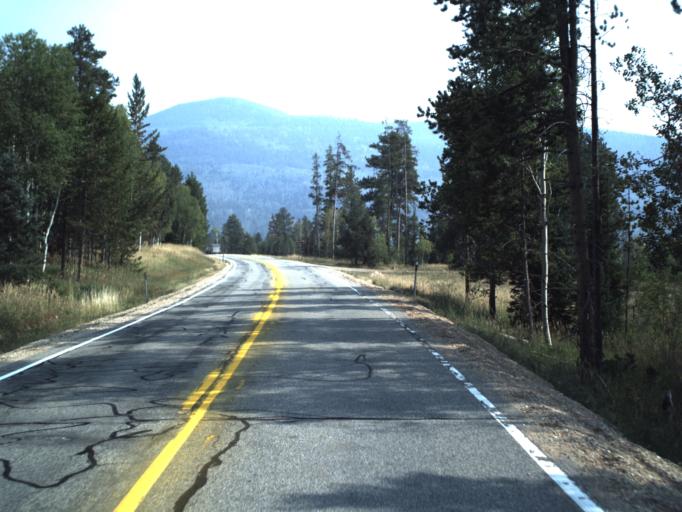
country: US
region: Utah
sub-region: Summit County
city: Francis
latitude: 40.6042
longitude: -111.1190
